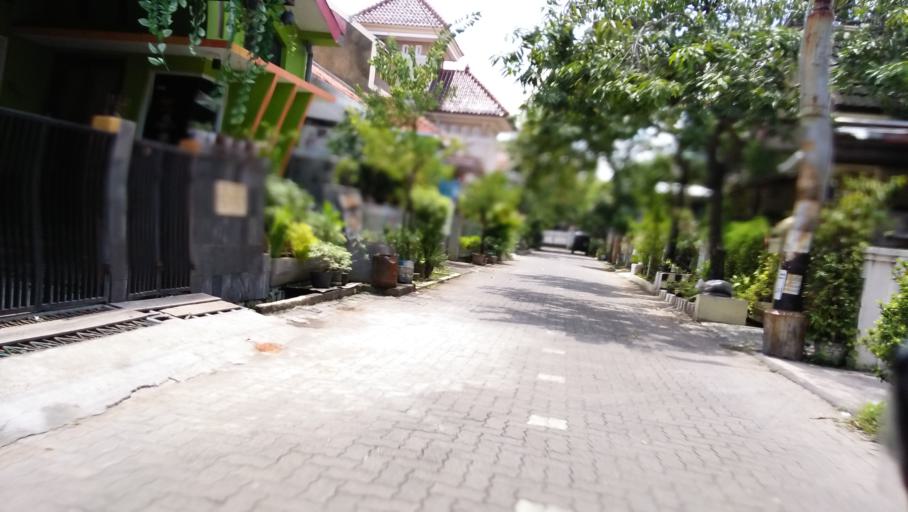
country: ID
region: Central Java
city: Mranggen
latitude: -7.0287
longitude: 110.4630
